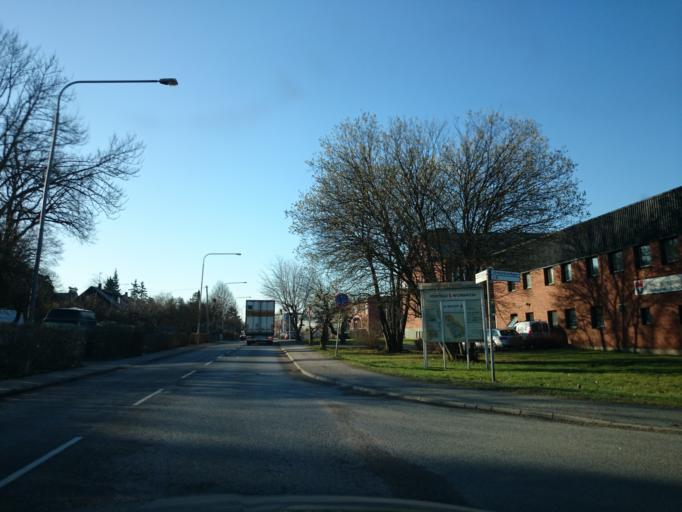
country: SE
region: Stockholm
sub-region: Huddinge Kommun
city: Segeltorp
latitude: 59.2835
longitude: 17.9476
